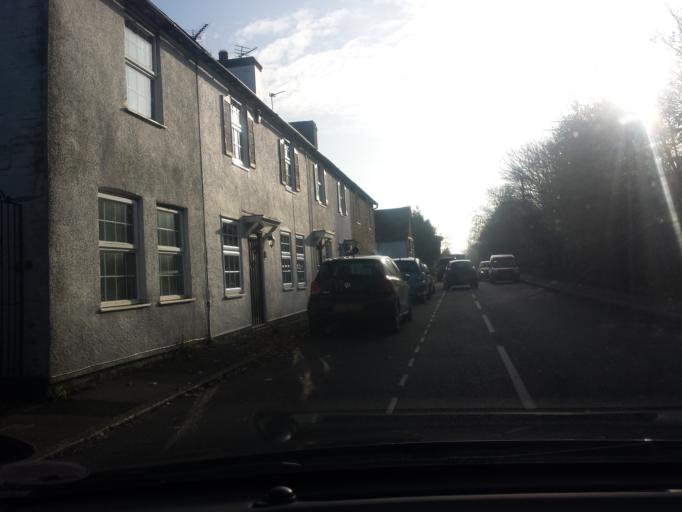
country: GB
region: England
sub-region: Essex
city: Saint Osyth
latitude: 51.8035
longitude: 1.0786
